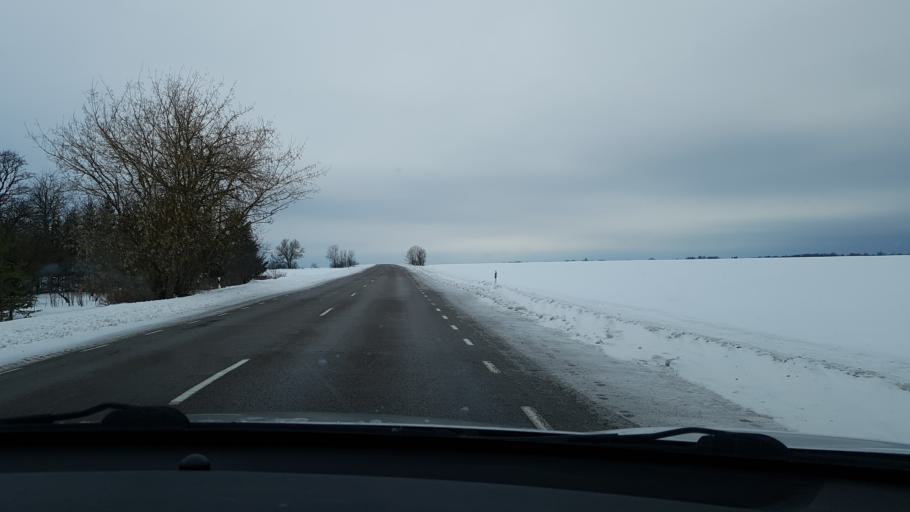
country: EE
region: Jaervamaa
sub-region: Paide linn
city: Paide
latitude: 58.8971
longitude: 25.7337
